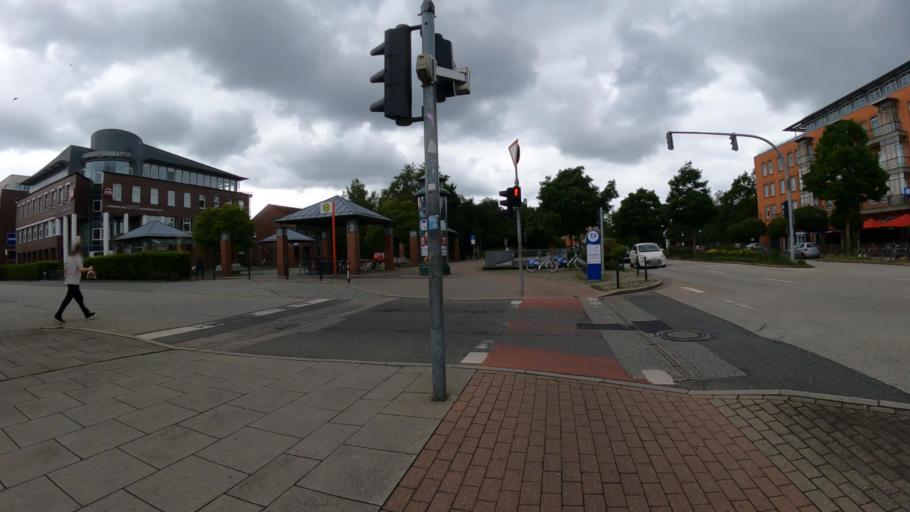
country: DE
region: Schleswig-Holstein
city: Norderstedt
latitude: 53.7073
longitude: 9.9925
